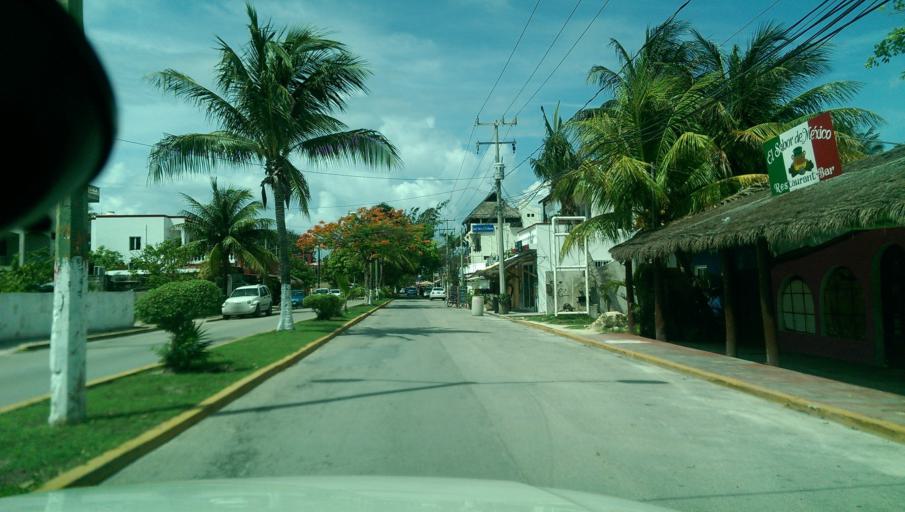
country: MX
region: Quintana Roo
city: Alfredo V. Bonfil
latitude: 20.8497
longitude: -86.8753
